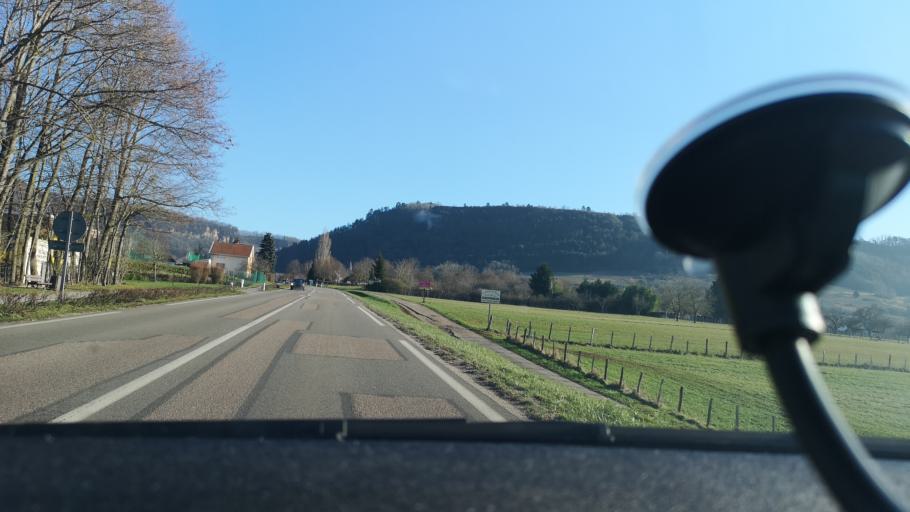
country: FR
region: Franche-Comte
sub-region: Departement du Jura
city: Poligny
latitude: 46.8357
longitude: 5.6941
